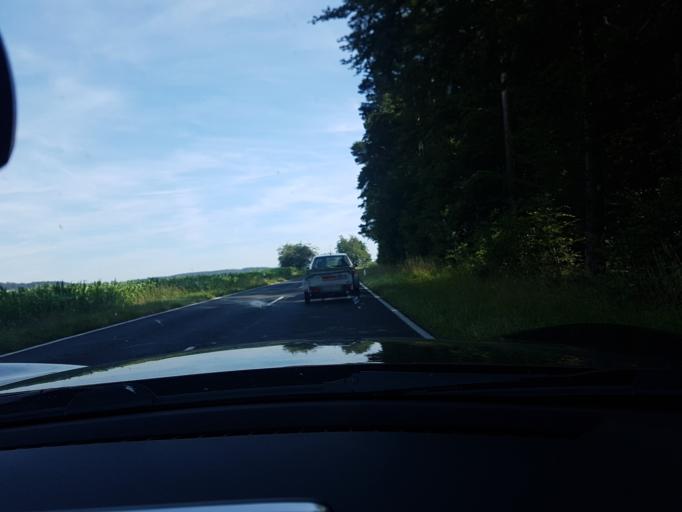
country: DE
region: Baden-Wuerttemberg
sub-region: Karlsruhe Region
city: Fahrenbach
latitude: 49.4432
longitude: 9.1549
